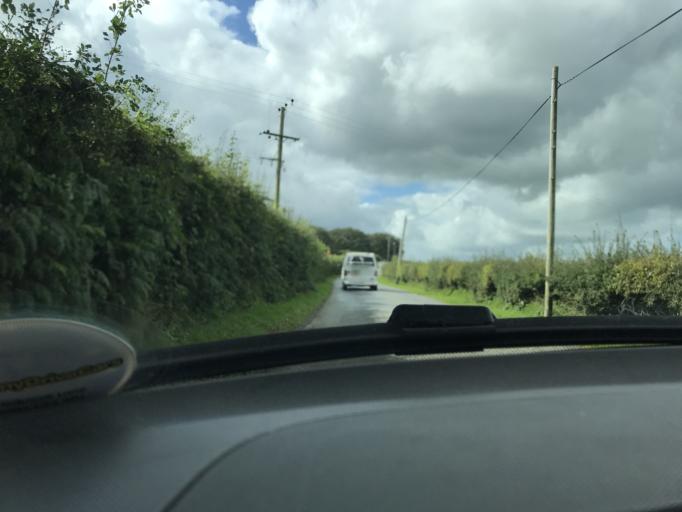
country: GB
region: England
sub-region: Devon
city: Horrabridge
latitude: 50.5393
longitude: -4.0943
